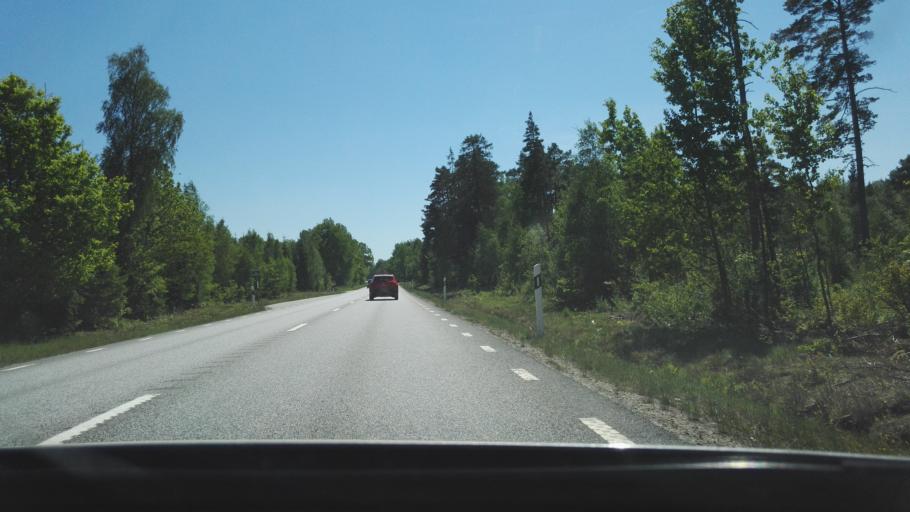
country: SE
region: Kronoberg
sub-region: Tingsryds Kommun
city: Tingsryd
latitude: 56.6040
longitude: 14.9273
